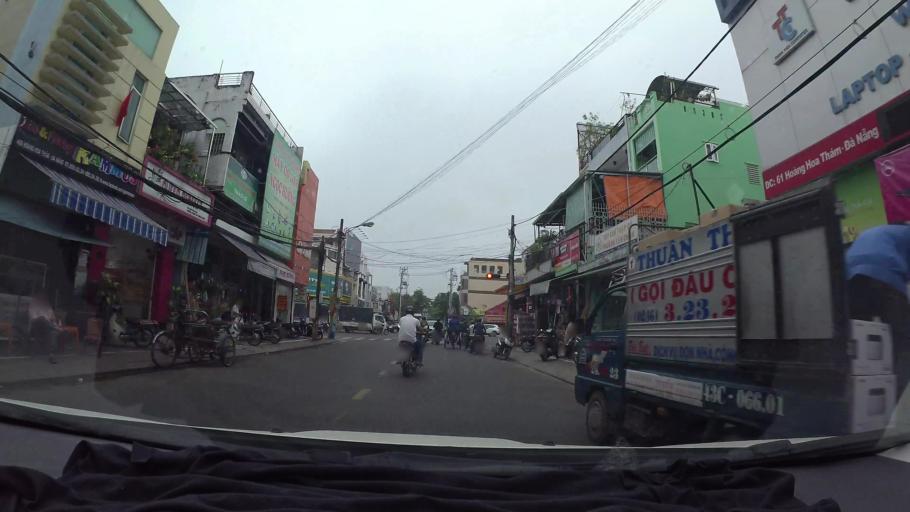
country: VN
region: Da Nang
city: Da Nang
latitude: 16.0690
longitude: 108.2098
